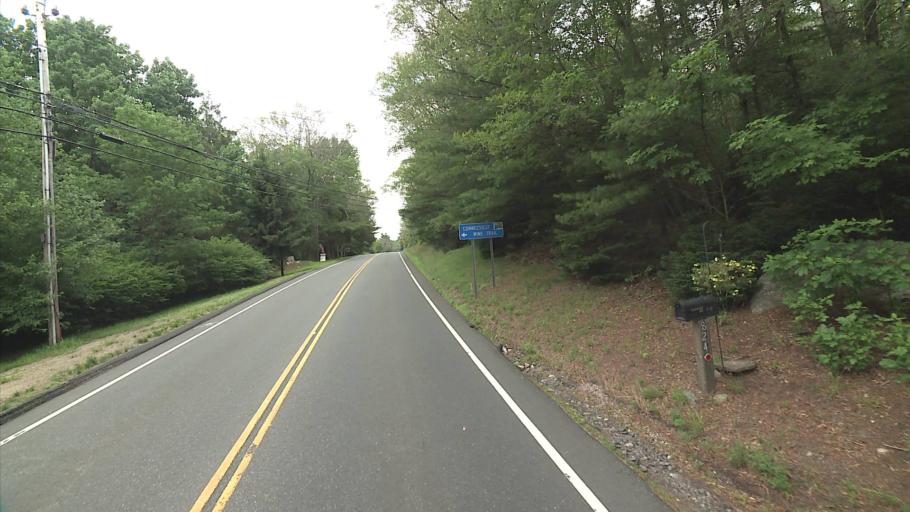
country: US
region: Connecticut
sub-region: New London County
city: Ledyard Center
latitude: 41.4537
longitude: -72.0167
